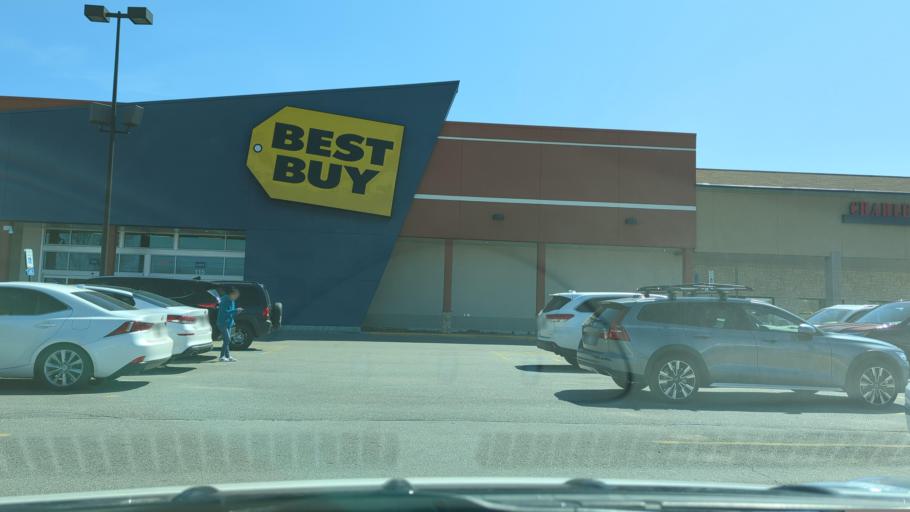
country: US
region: Nebraska
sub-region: Douglas County
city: Ralston
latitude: 41.2605
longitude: -96.0312
